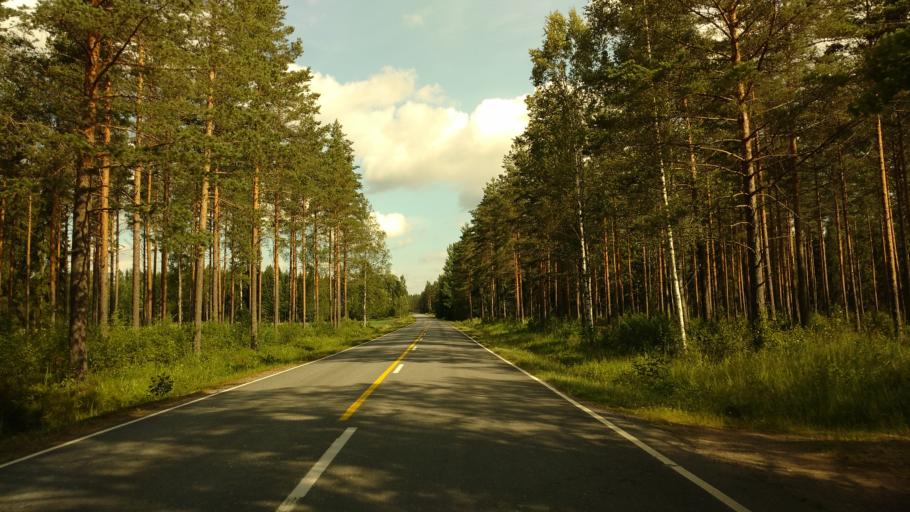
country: FI
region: Varsinais-Suomi
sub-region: Loimaa
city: Koski Tl
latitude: 60.6053
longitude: 23.1233
